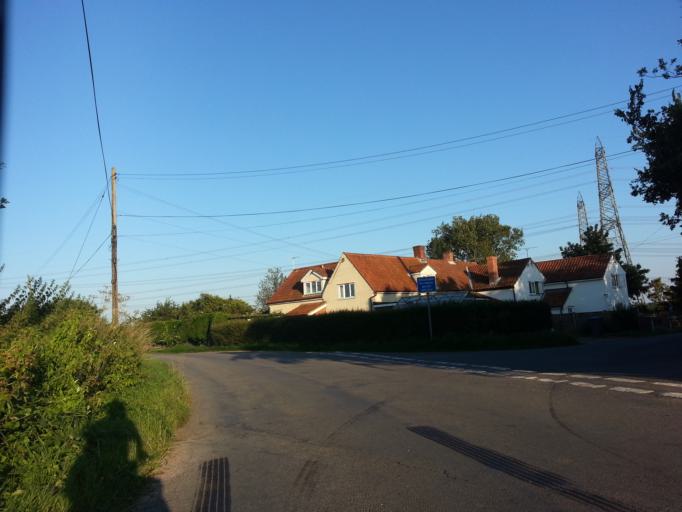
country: GB
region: England
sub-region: Suffolk
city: Kesgrave
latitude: 52.1162
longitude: 1.2333
